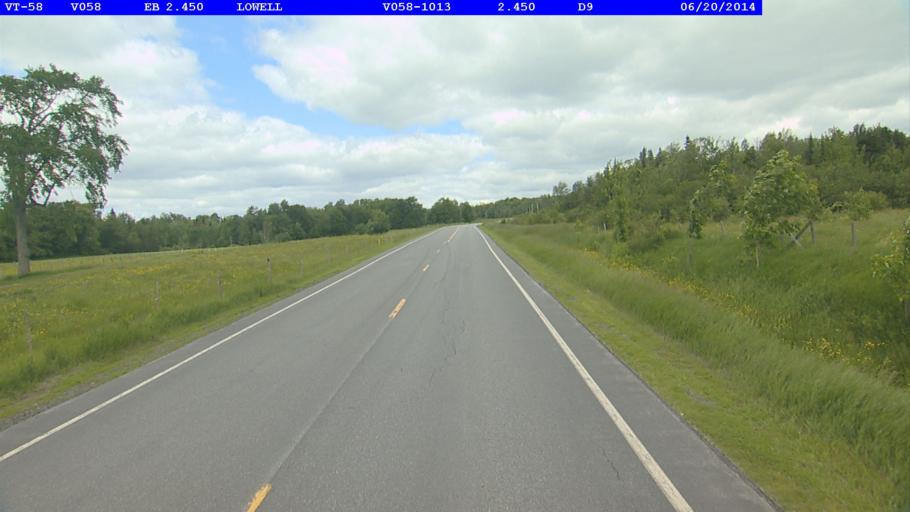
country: US
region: Vermont
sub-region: Orleans County
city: Newport
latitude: 44.8098
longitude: -72.4073
